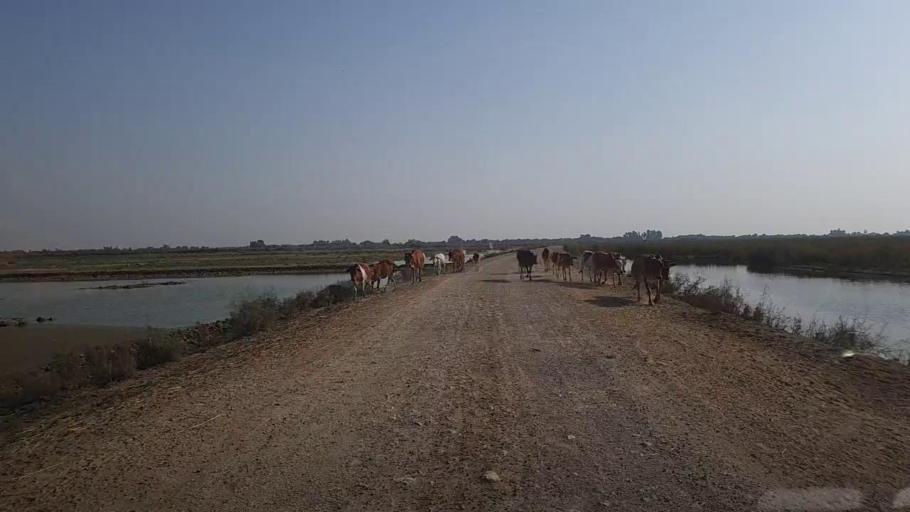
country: PK
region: Sindh
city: Kandhkot
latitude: 28.3634
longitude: 69.3300
